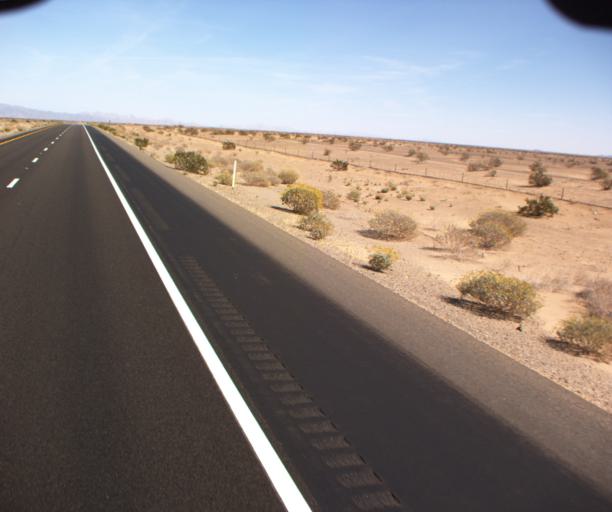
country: US
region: Arizona
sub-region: Yuma County
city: Somerton
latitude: 32.4951
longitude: -114.5833
